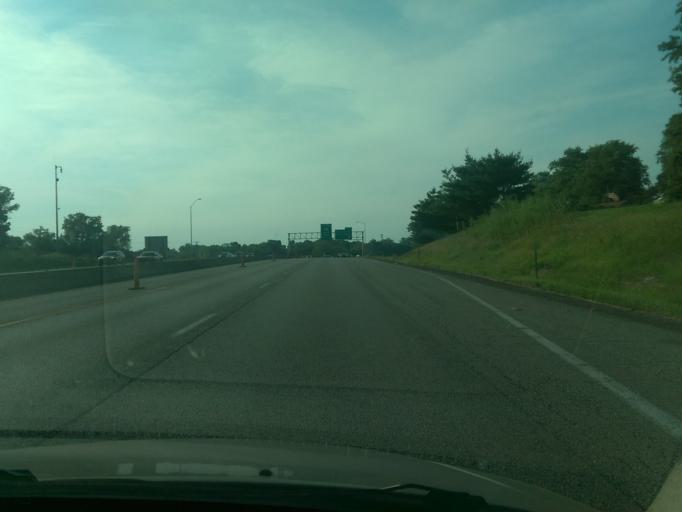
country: US
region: Missouri
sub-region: Platte County
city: Parkville
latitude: 39.2207
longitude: -94.6475
